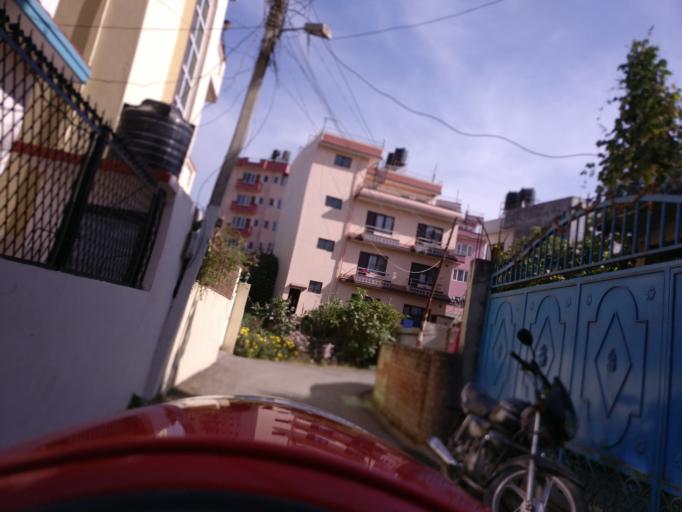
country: NP
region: Central Region
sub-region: Bagmati Zone
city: Patan
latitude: 27.6587
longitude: 85.3099
